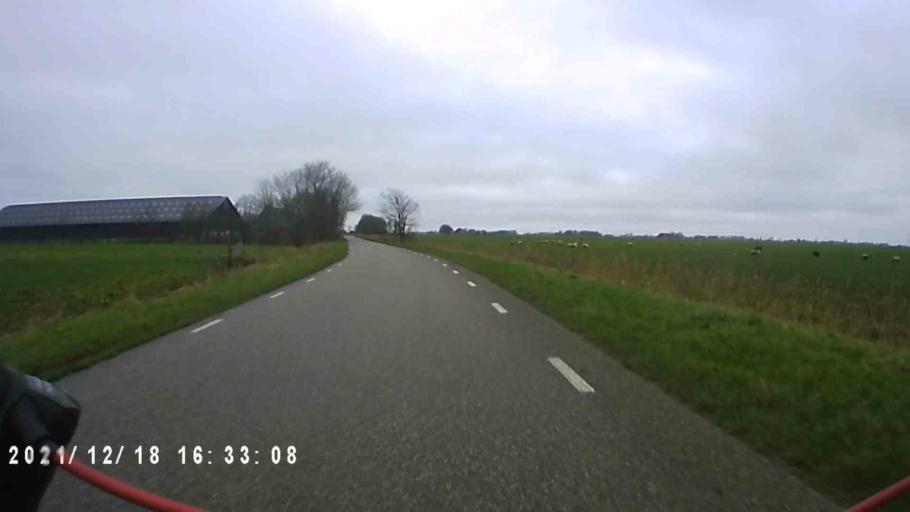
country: NL
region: Friesland
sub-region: Gemeente Dongeradeel
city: Dokkum
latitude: 53.3565
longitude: 6.0310
